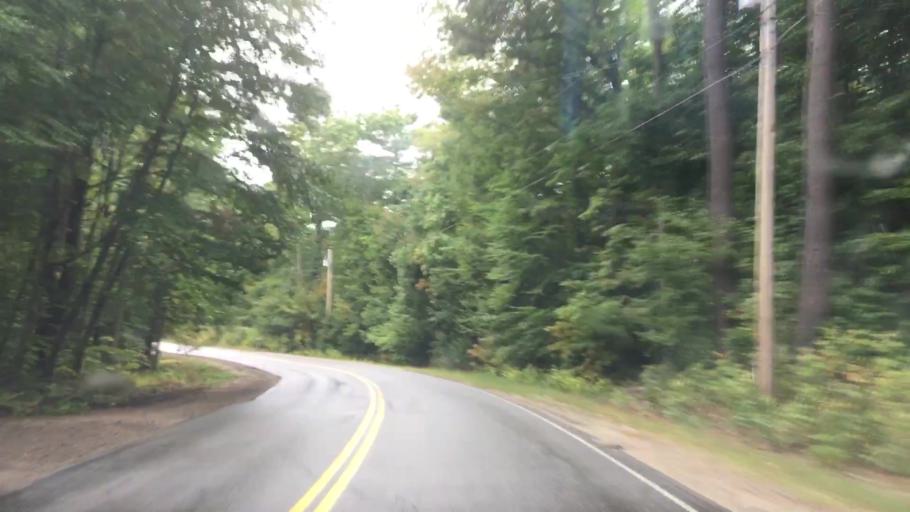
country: US
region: Maine
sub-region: Cumberland County
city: Raymond
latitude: 43.9340
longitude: -70.4129
